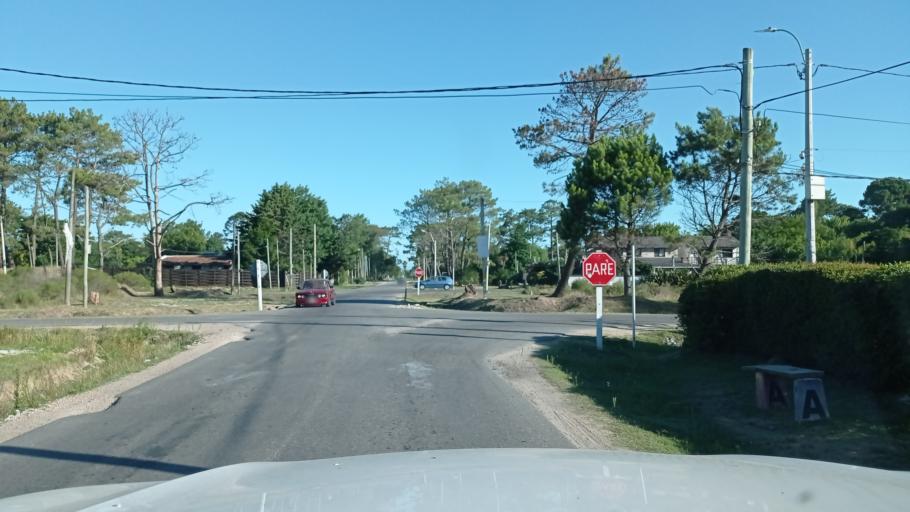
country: UY
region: Canelones
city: Pando
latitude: -34.7993
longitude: -55.9058
